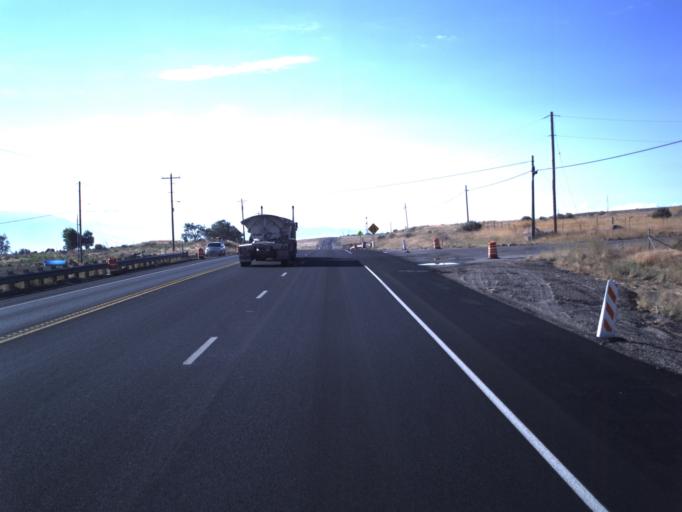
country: US
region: Utah
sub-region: Salt Lake County
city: Oquirrh
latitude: 40.6468
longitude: -112.0682
